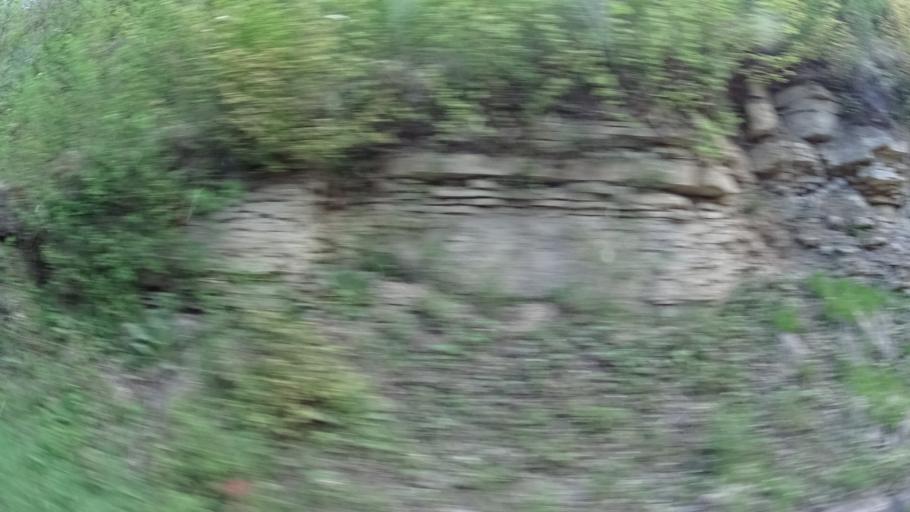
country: DE
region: Baden-Wuerttemberg
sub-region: Tuebingen Region
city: Haigerloch
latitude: 48.3713
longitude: 8.8010
